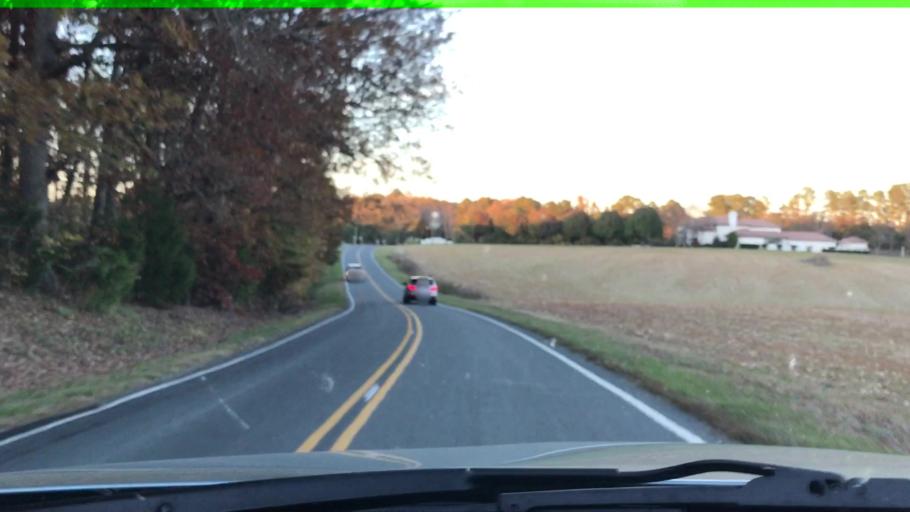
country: US
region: North Carolina
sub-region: Union County
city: Wesley Chapel
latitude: 34.9932
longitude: -80.7136
